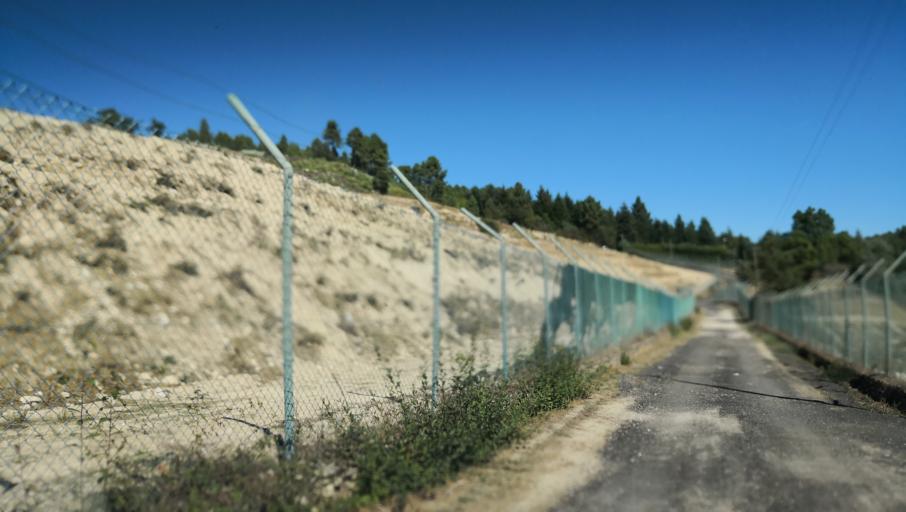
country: PT
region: Vila Real
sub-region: Vila Real
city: Vila Real
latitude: 41.3219
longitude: -7.7236
